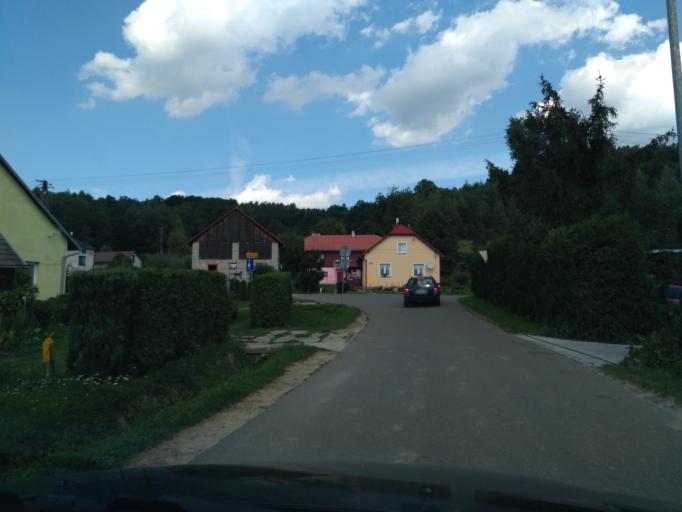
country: PL
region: Subcarpathian Voivodeship
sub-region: Powiat strzyzowski
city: Strzyzow
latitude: 49.8438
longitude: 21.8237
